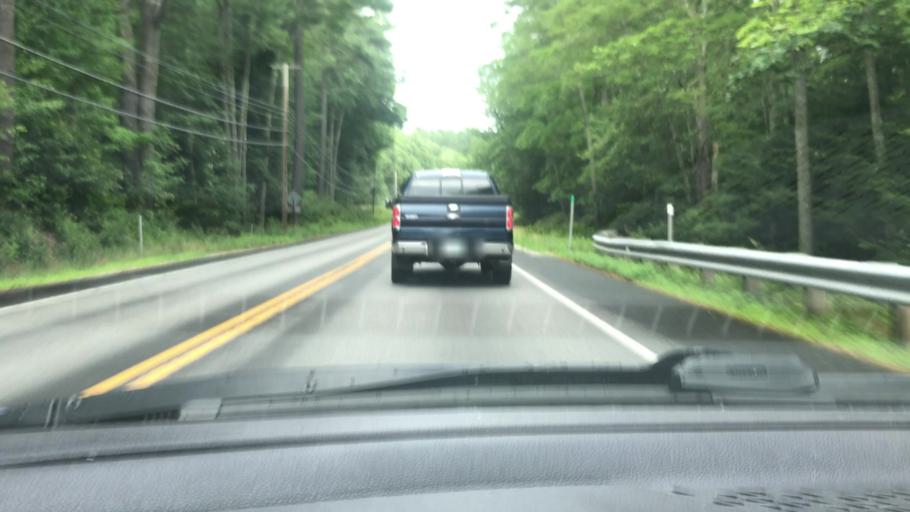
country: US
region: New Hampshire
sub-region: Merrimack County
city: Epsom
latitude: 43.2242
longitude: -71.3149
